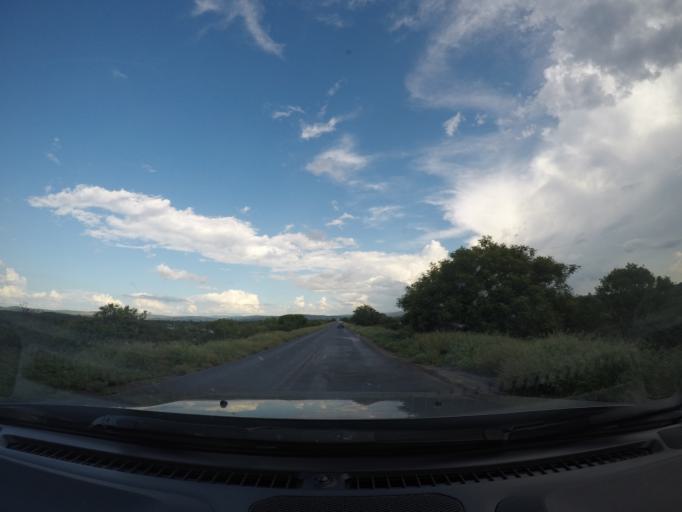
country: BR
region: Bahia
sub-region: Ibotirama
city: Ibotirama
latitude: -12.1707
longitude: -43.2645
